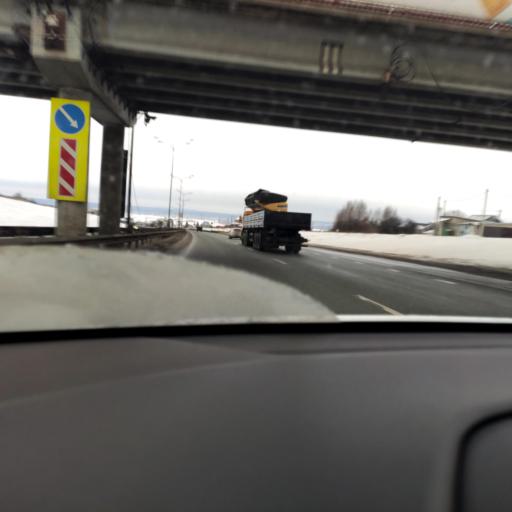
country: RU
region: Tatarstan
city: Osinovo
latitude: 55.7733
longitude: 48.8386
